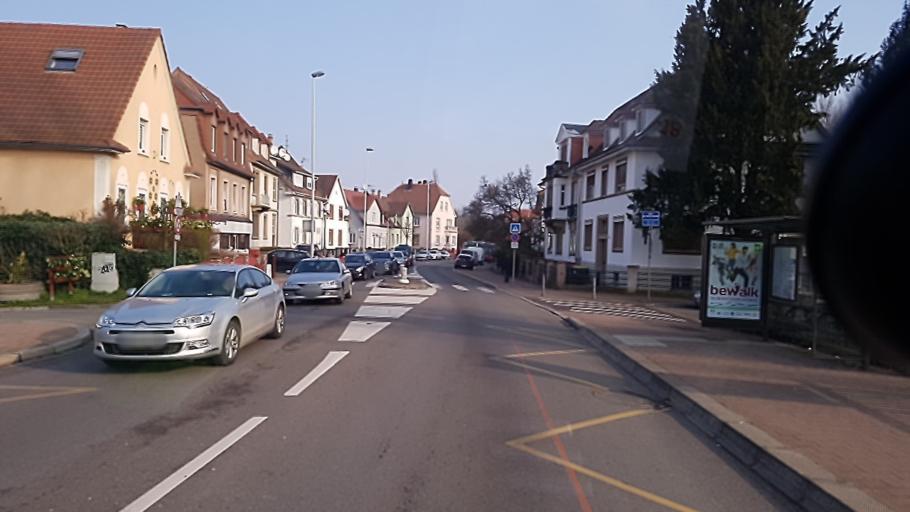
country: FR
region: Alsace
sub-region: Departement du Bas-Rhin
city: Eckbolsheim
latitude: 48.5700
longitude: 7.7111
